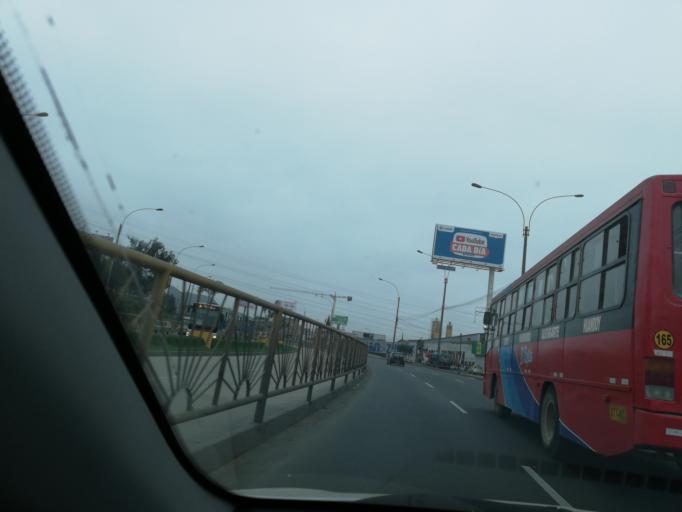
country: PE
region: Lima
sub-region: Lima
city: Independencia
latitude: -11.9922
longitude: -77.0574
